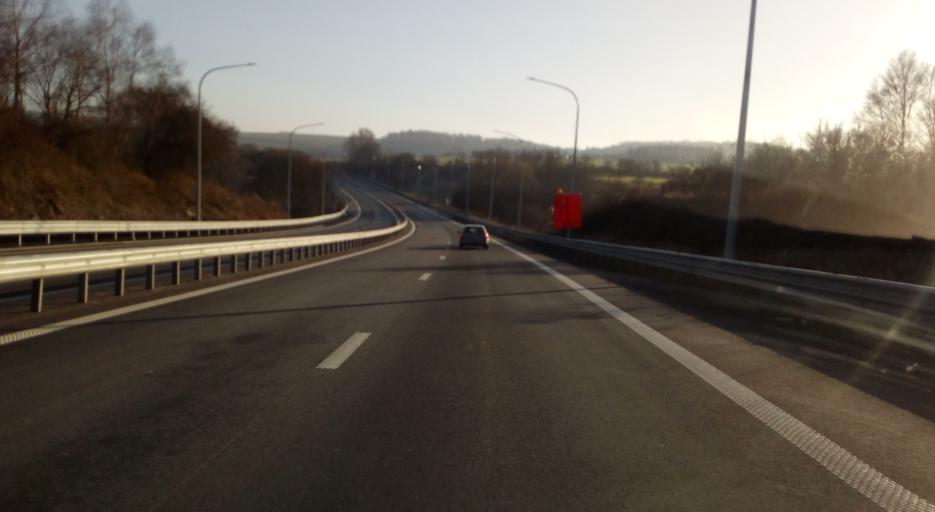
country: BE
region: Wallonia
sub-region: Province de Namur
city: Walcourt
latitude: 50.2843
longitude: 4.4813
